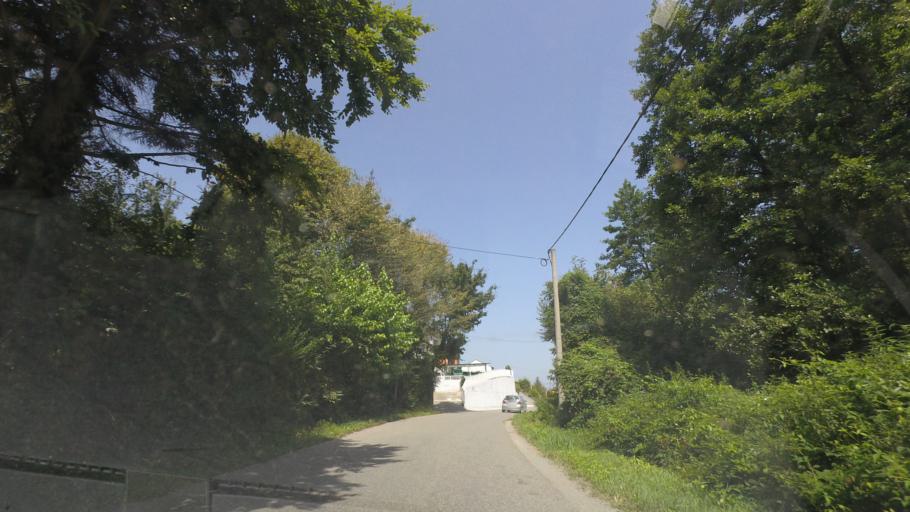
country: HR
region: Karlovacka
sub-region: Grad Karlovac
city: Karlovac
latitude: 45.5145
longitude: 15.5216
